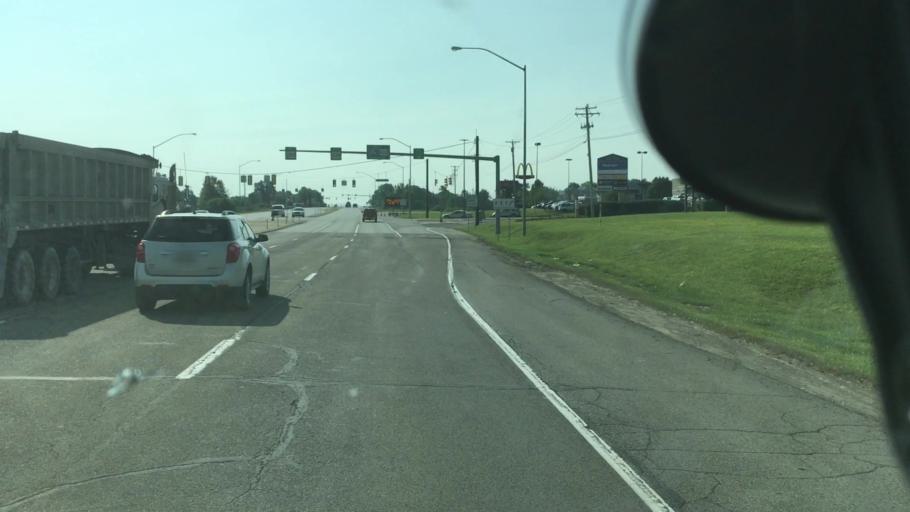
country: US
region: Pennsylvania
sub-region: Lawrence County
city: Oakwood
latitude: 41.0124
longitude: -80.3954
